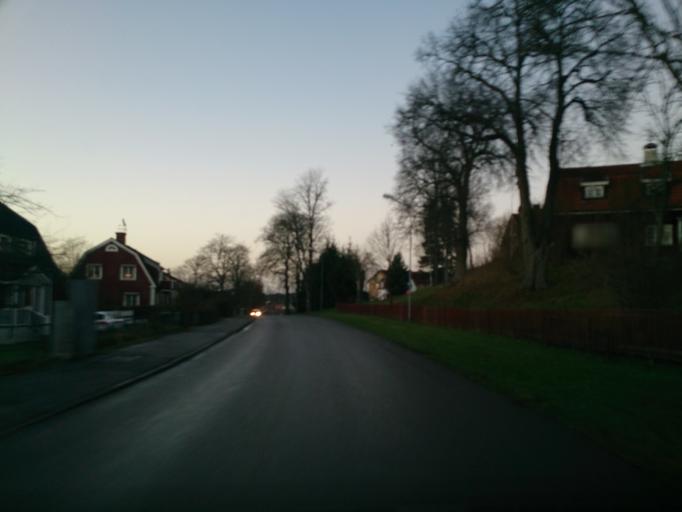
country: SE
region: OEstergoetland
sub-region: Atvidabergs Kommun
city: Atvidaberg
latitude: 58.1956
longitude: 16.0077
